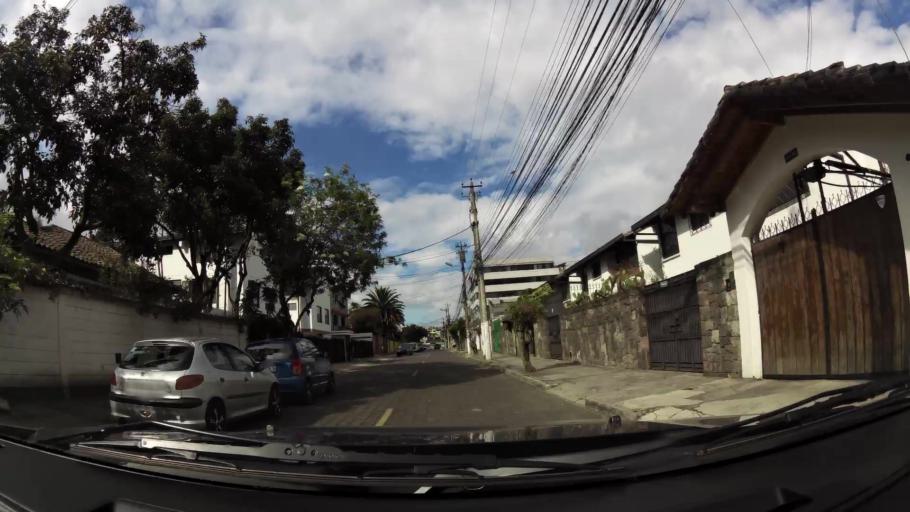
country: EC
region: Pichincha
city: Quito
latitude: -0.1588
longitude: -78.4791
